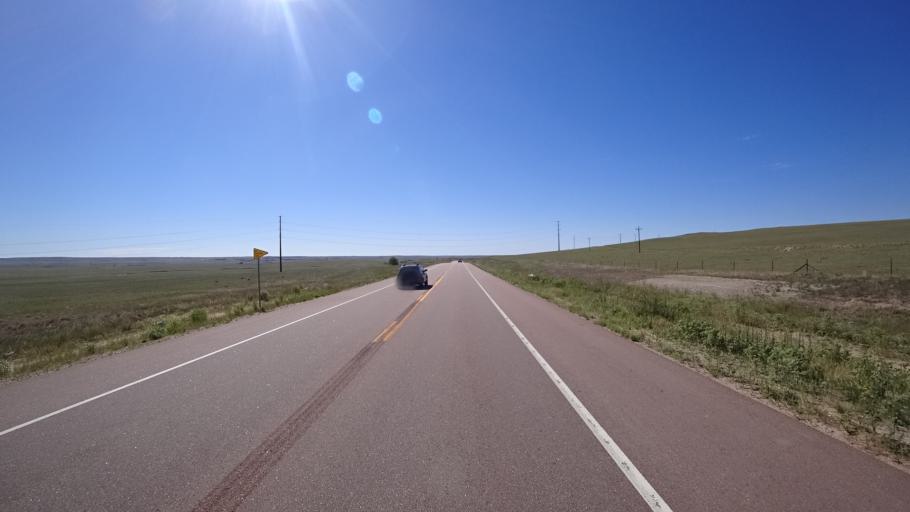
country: US
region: Colorado
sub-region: El Paso County
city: Cimarron Hills
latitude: 38.8057
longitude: -104.6671
